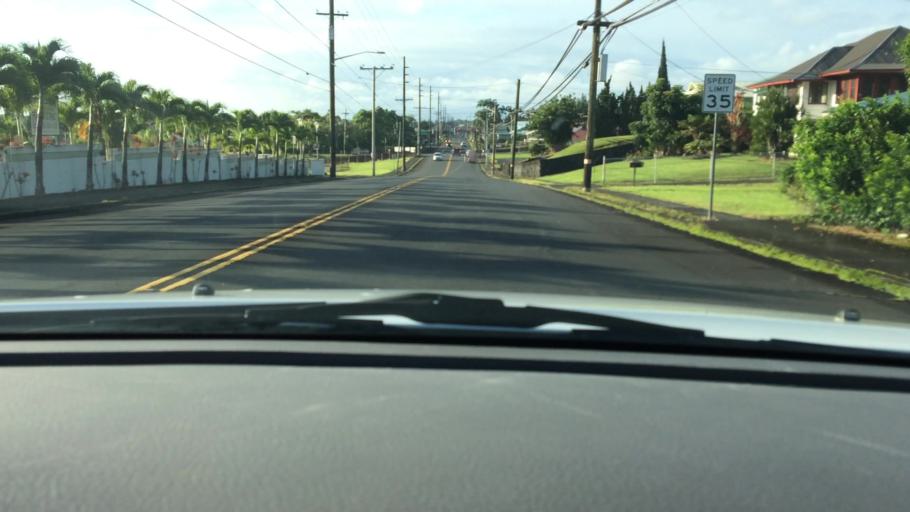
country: US
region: Hawaii
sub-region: Hawaii County
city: Hilo
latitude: 19.7136
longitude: -155.0817
